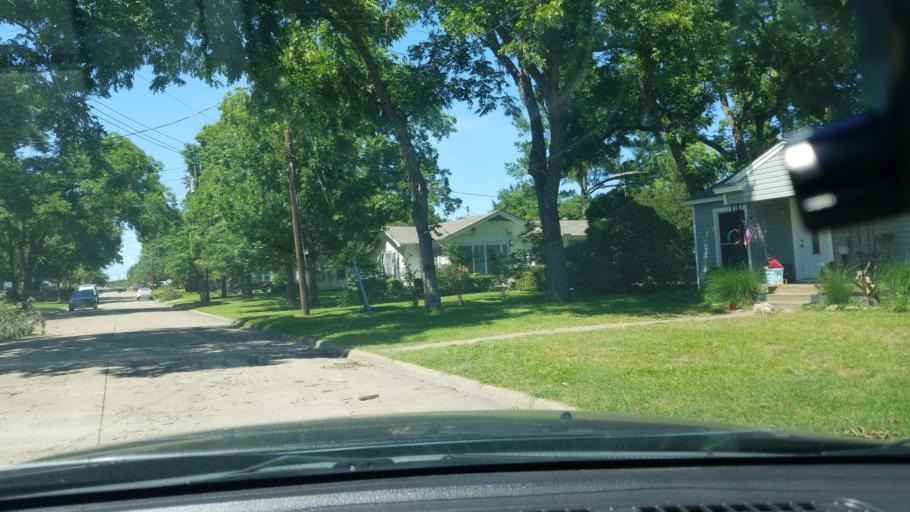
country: US
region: Texas
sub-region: Dallas County
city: Mesquite
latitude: 32.7627
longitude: -96.6034
